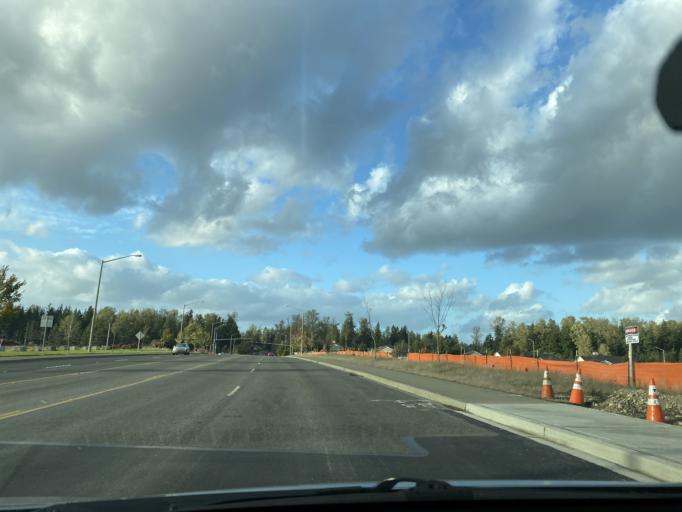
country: US
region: Washington
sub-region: Pierce County
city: South Hill
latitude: 47.0961
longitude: -122.2643
